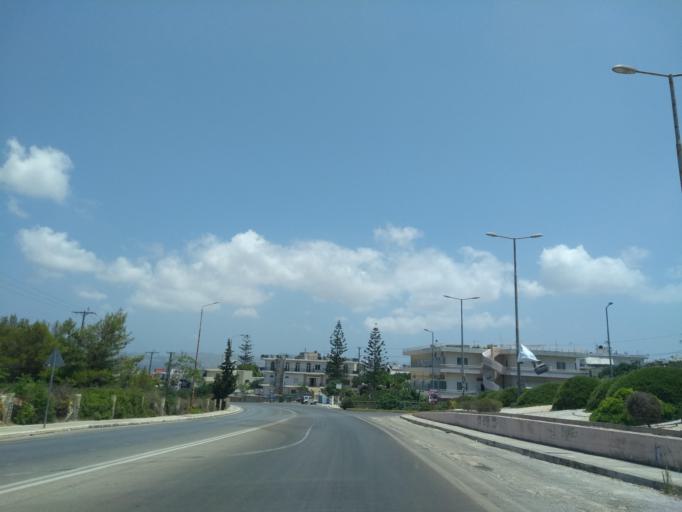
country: GR
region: Crete
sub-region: Nomos Chanias
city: Pithari
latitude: 35.5264
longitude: 24.0717
